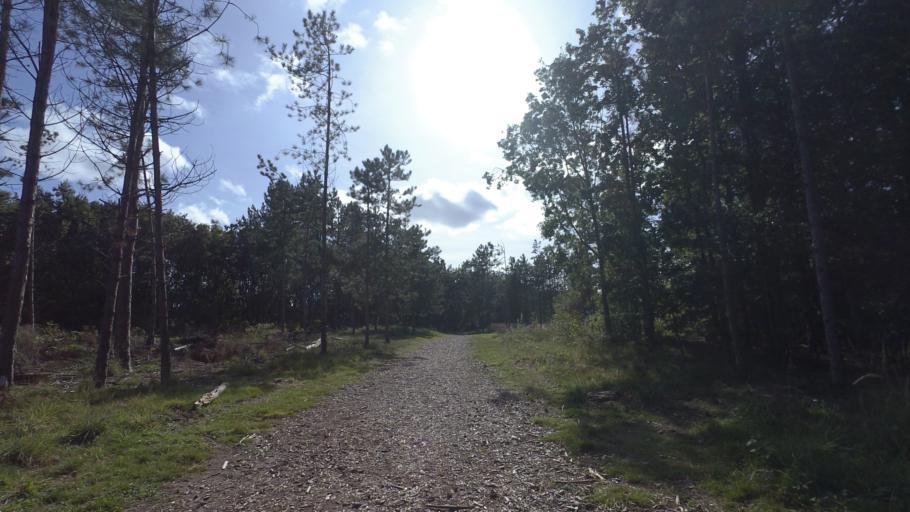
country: NL
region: Friesland
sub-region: Gemeente Ameland
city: Hollum
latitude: 53.4502
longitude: 5.6959
